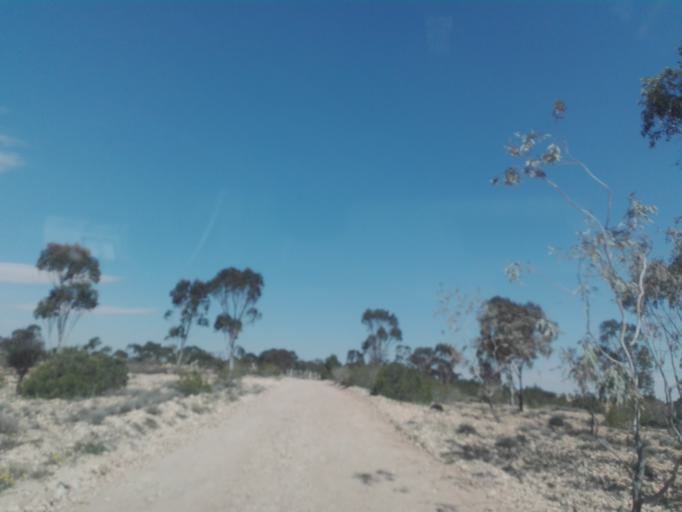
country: TN
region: Safaqis
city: Sfax
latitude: 34.7015
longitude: 10.5293
